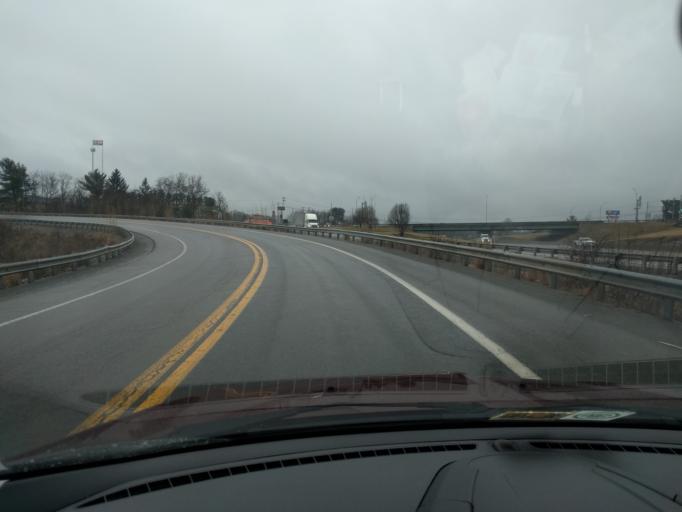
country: US
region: West Virginia
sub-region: Raleigh County
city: Mabscott
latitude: 37.7944
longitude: -81.2146
